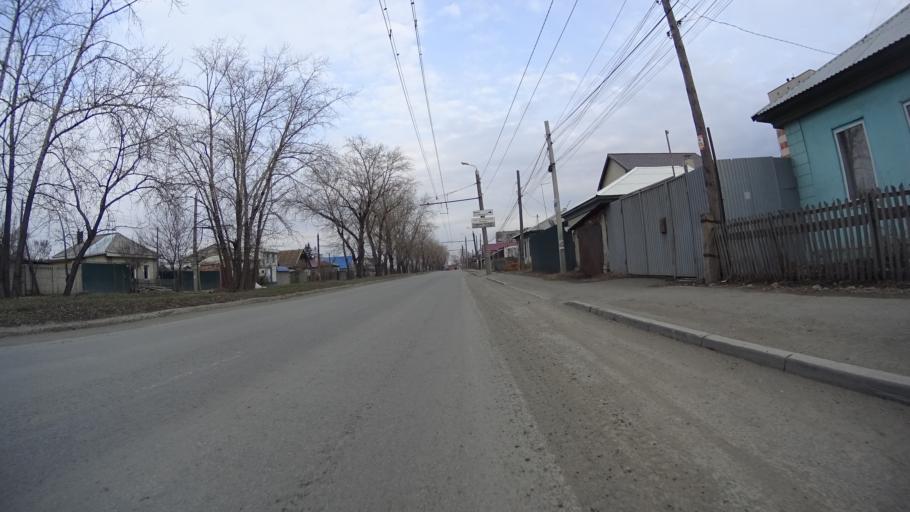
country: RU
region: Chelyabinsk
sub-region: Gorod Chelyabinsk
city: Chelyabinsk
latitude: 55.1918
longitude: 61.4704
